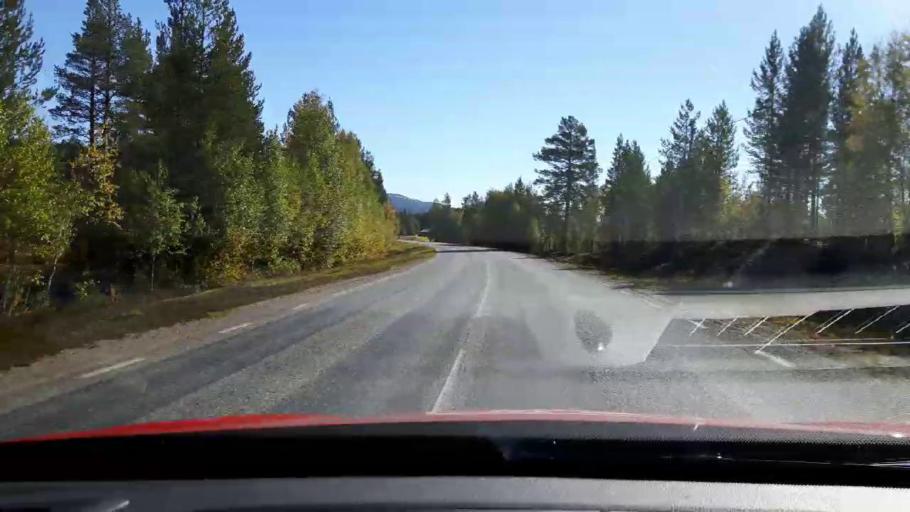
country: SE
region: Jaemtland
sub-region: Harjedalens Kommun
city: Sveg
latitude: 62.3641
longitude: 13.9962
